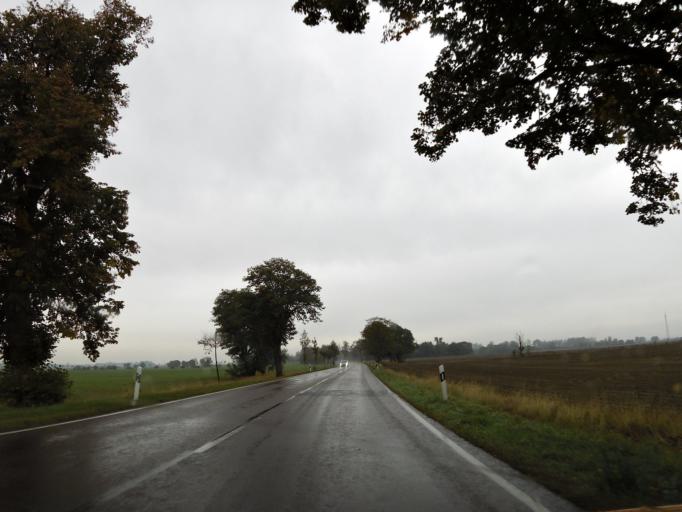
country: DE
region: Saxony-Anhalt
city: Quellendorf
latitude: 51.7903
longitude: 12.1035
